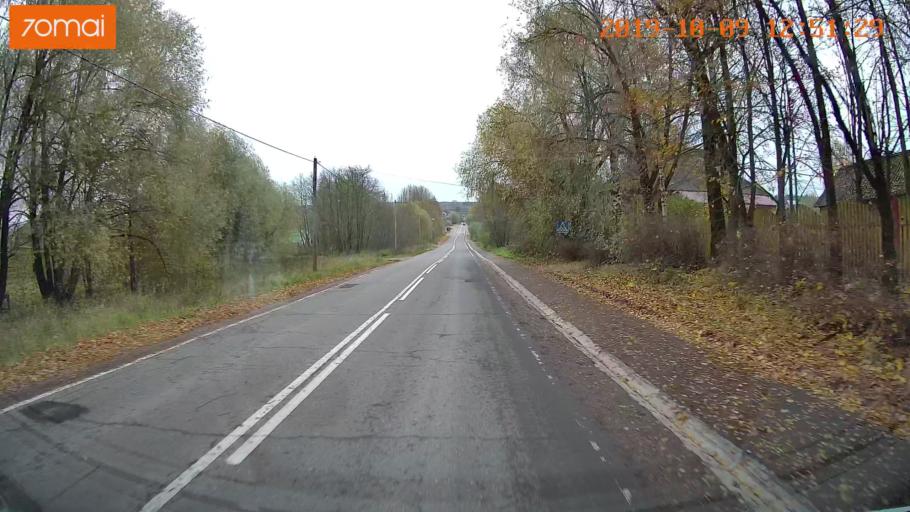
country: RU
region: Jaroslavl
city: Prechistoye
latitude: 58.4193
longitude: 40.3423
